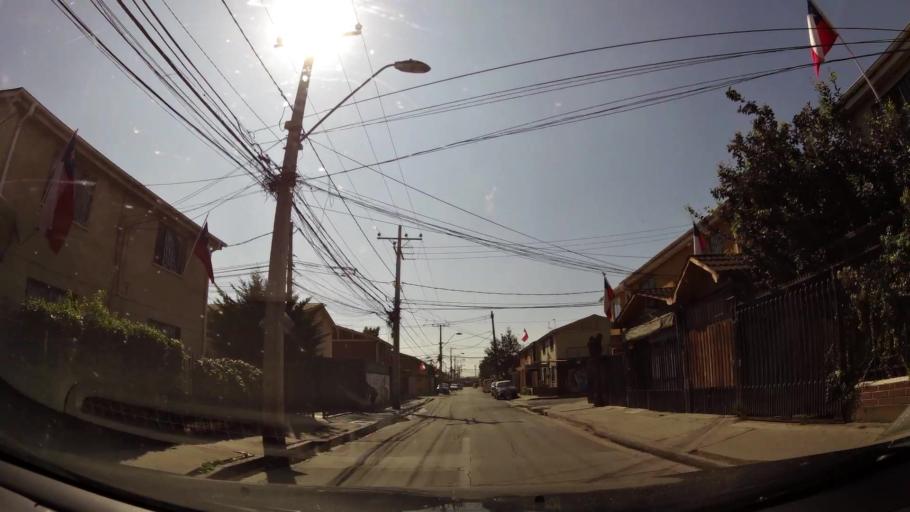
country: CL
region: Santiago Metropolitan
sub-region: Provincia de Santiago
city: Lo Prado
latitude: -33.3595
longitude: -70.7525
